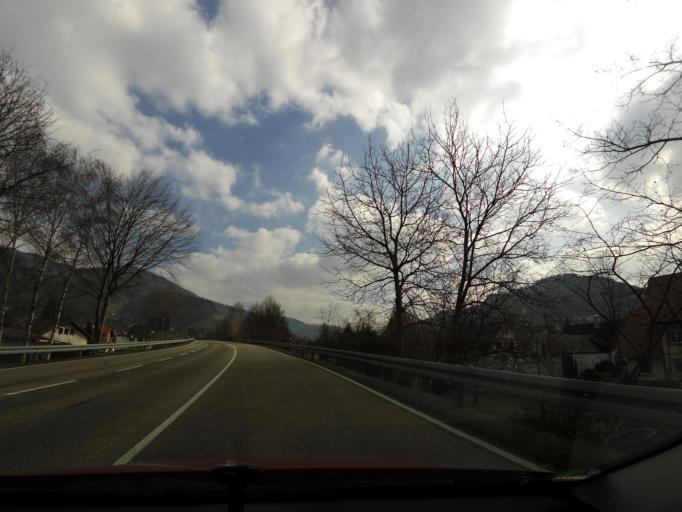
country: DE
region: Baden-Wuerttemberg
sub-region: Freiburg Region
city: Kappelrodeck
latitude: 48.5946
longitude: 8.1115
